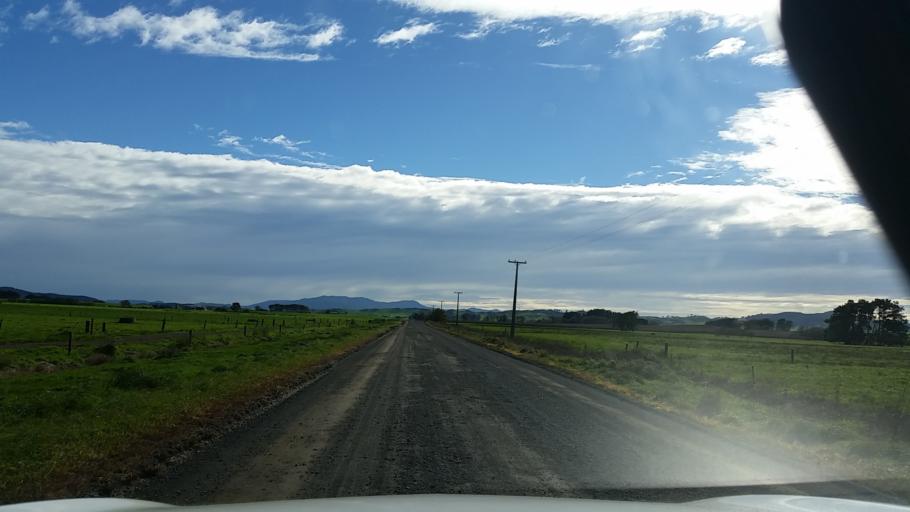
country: NZ
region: Waikato
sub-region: Hamilton City
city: Hamilton
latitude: -37.6397
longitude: 175.4310
